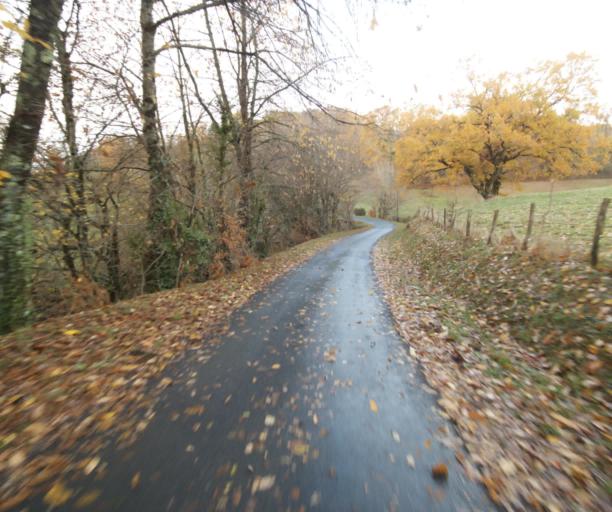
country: FR
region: Limousin
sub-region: Departement de la Correze
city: Cornil
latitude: 45.2159
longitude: 1.6677
